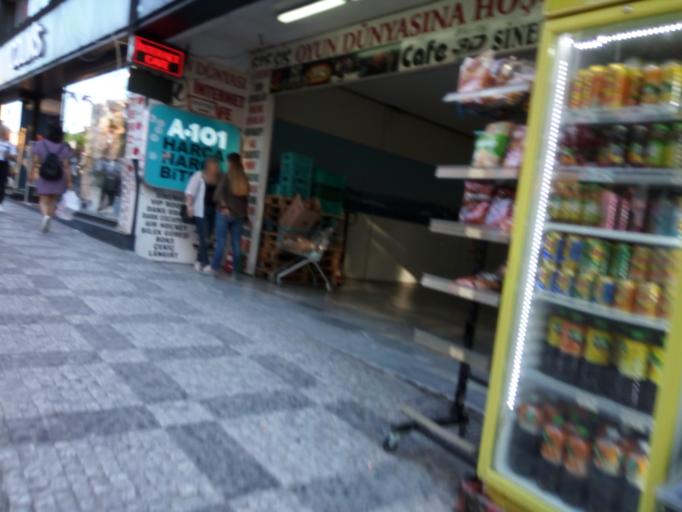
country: TR
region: Istanbul
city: UEskuedar
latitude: 40.9917
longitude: 29.0285
